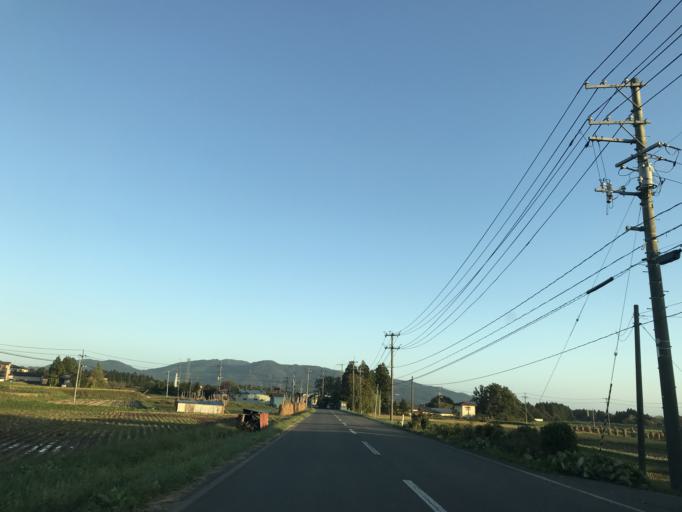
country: JP
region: Iwate
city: Mizusawa
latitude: 39.0572
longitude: 141.1120
